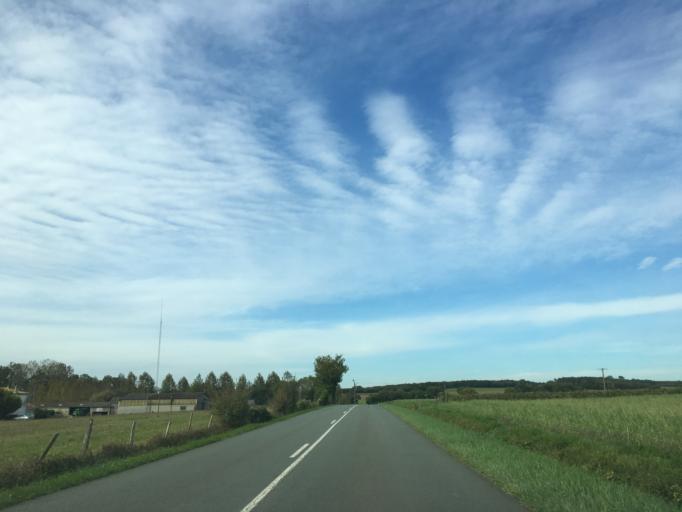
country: FR
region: Poitou-Charentes
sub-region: Departement de la Charente-Maritime
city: Aulnay
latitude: 46.0694
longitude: -0.4286
